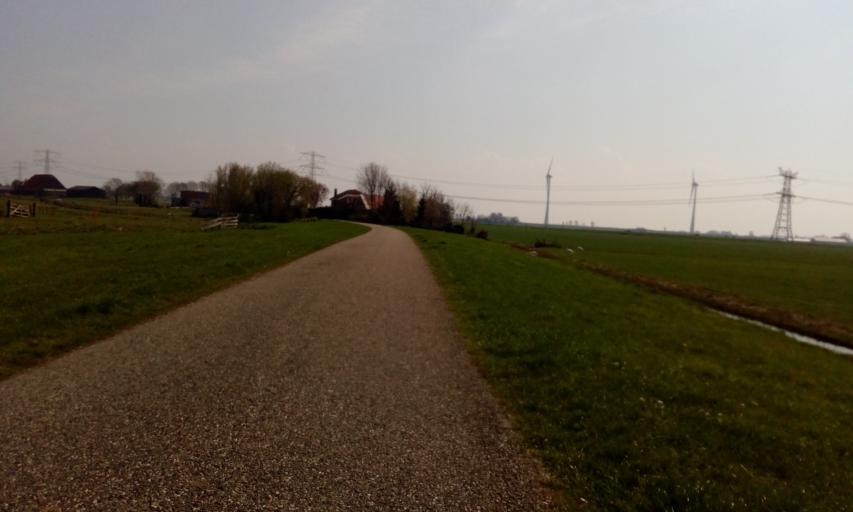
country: NL
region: South Holland
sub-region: Gemeente Spijkenisse
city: Spijkenisse
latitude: 51.8265
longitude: 4.3177
